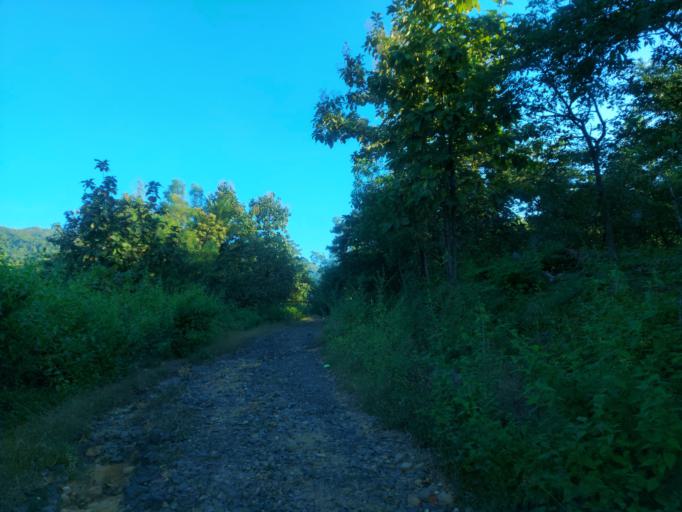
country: IN
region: Maharashtra
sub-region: Sindhudurg
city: Kudal
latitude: 16.0735
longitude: 73.8256
